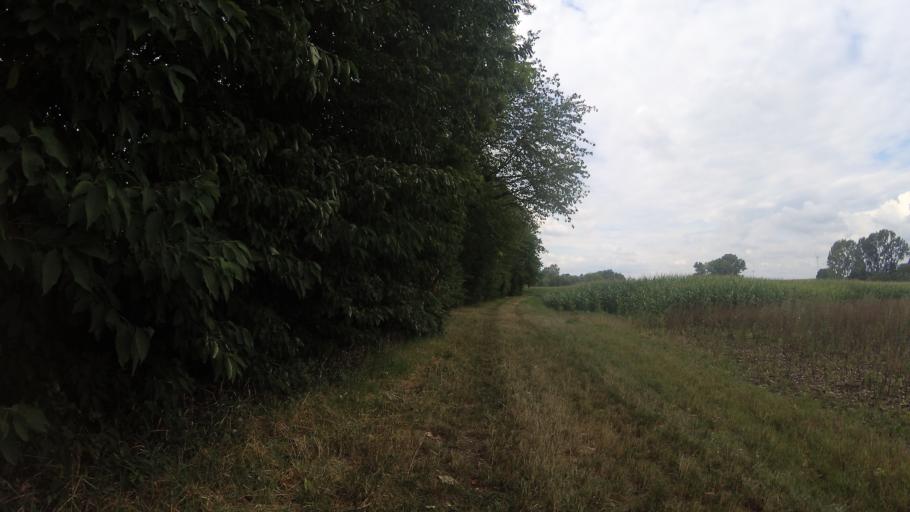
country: DE
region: Rheinland-Pfalz
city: Lingenfeld
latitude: 49.2621
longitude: 8.3794
